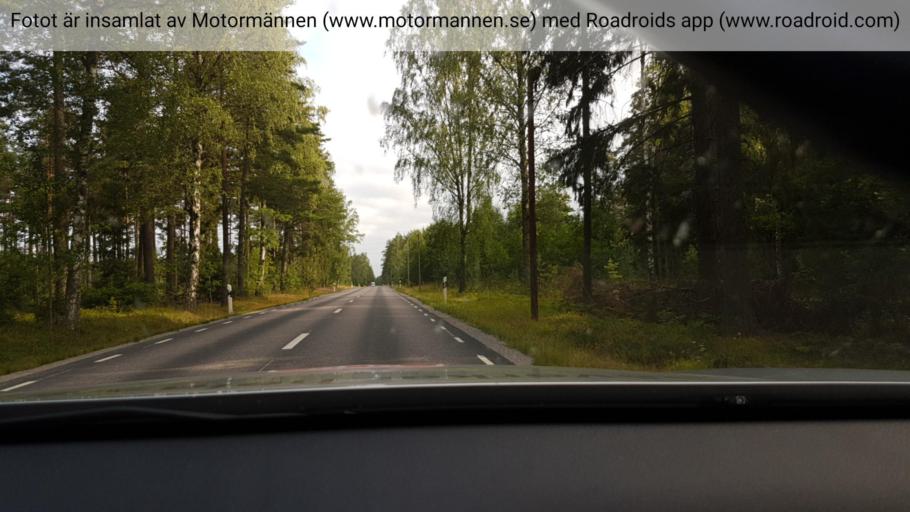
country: SE
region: Stockholm
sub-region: Norrtalje Kommun
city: Rimbo
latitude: 59.7792
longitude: 18.4362
